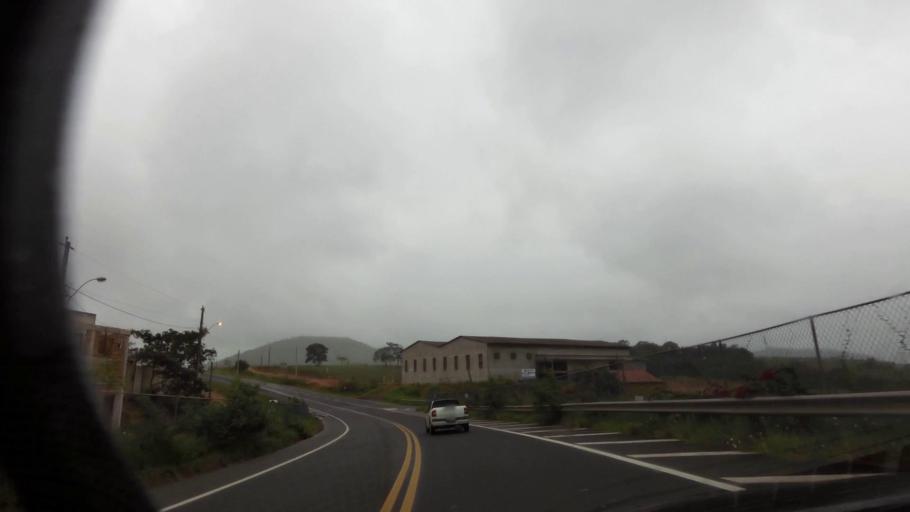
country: BR
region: Espirito Santo
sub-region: Guarapari
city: Guarapari
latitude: -20.7298
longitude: -40.5589
